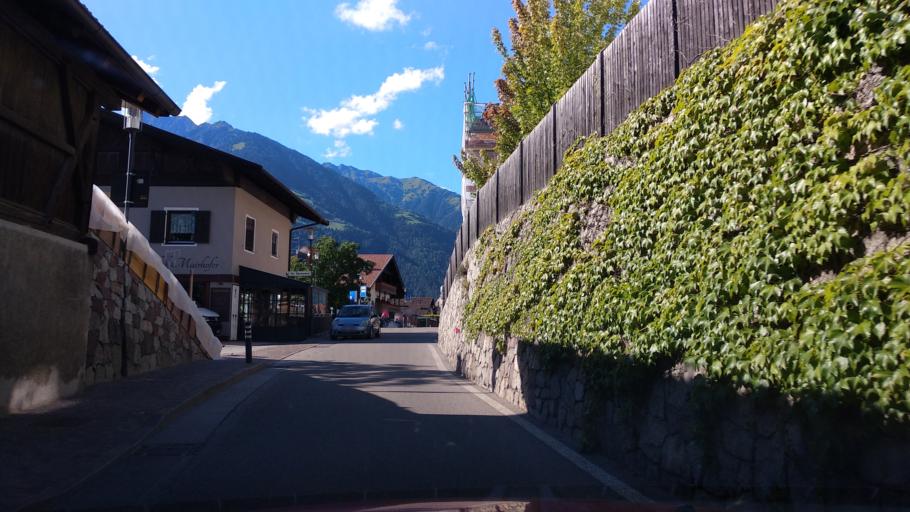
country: IT
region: Trentino-Alto Adige
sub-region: Bolzano
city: Scena
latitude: 46.6851
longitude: 11.1891
